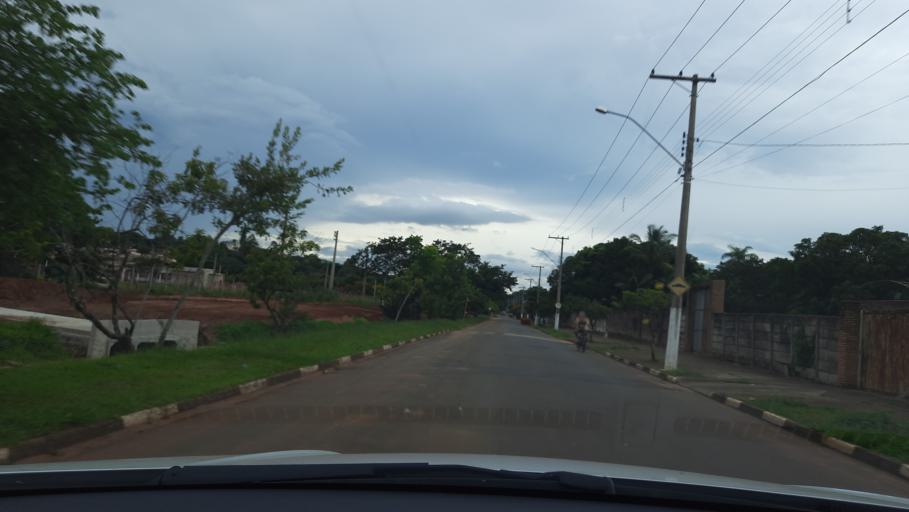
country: BR
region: Sao Paulo
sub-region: Casa Branca
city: Casa Branca
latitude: -21.7678
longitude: -47.0885
